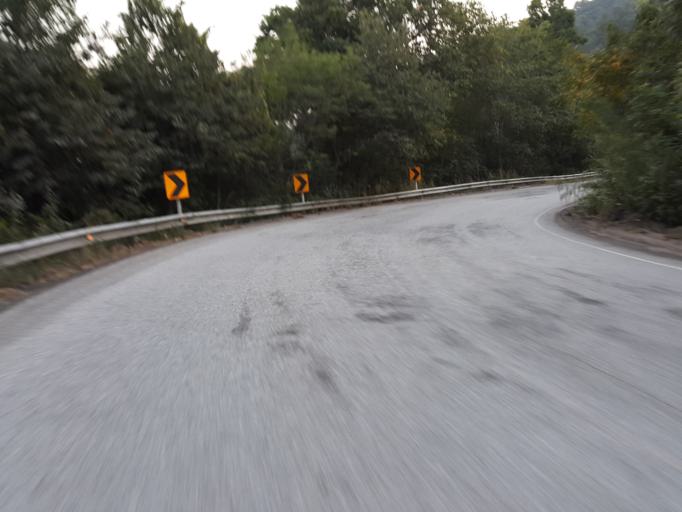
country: TH
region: Lampang
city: Thoen
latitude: 17.6754
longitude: 99.1112
